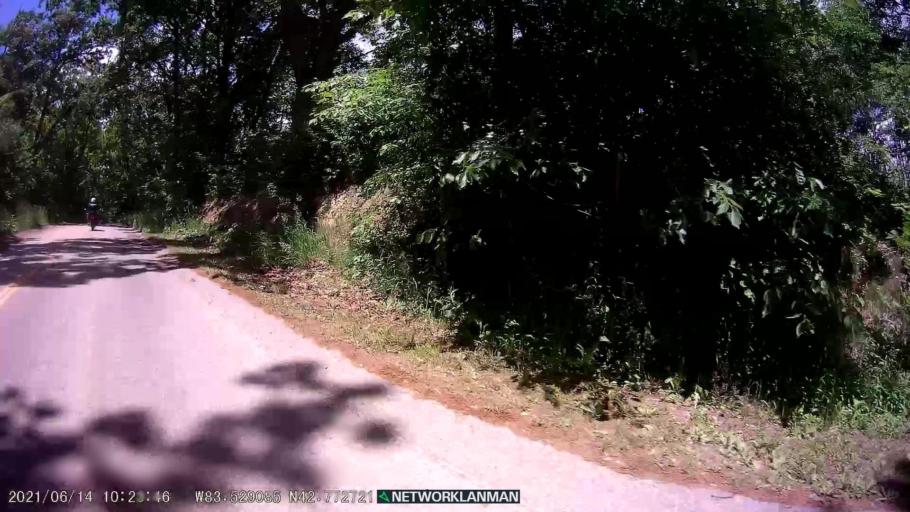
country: US
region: Michigan
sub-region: Oakland County
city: Holly
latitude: 42.7727
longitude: -83.5293
